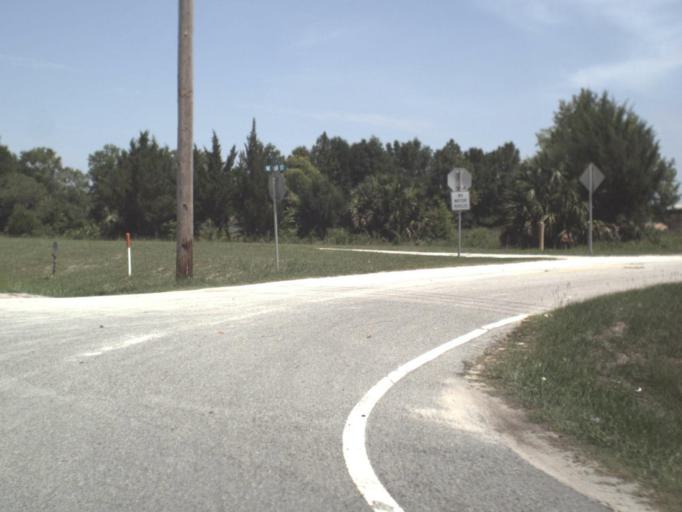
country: US
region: Florida
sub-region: Dixie County
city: Cross City
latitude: 29.6267
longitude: -83.1116
